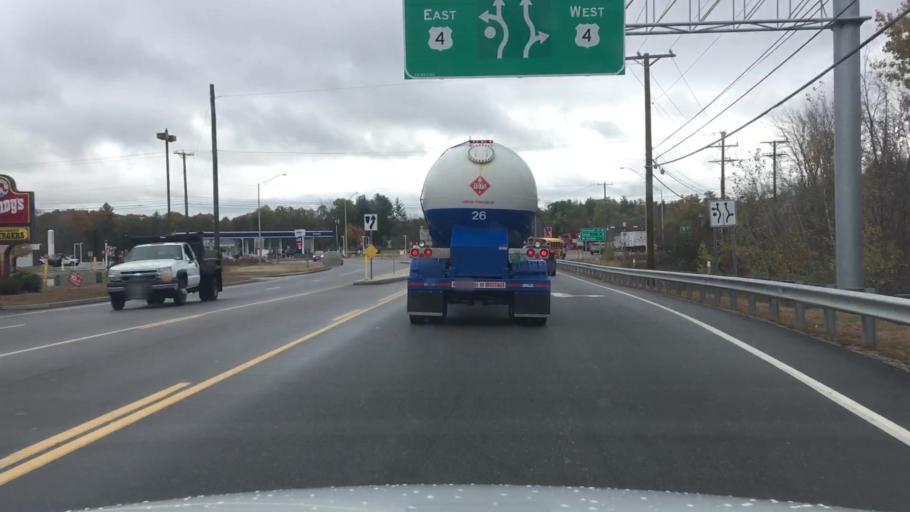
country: US
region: New Hampshire
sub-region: Strafford County
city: Lee
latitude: 43.1503
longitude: -71.0063
